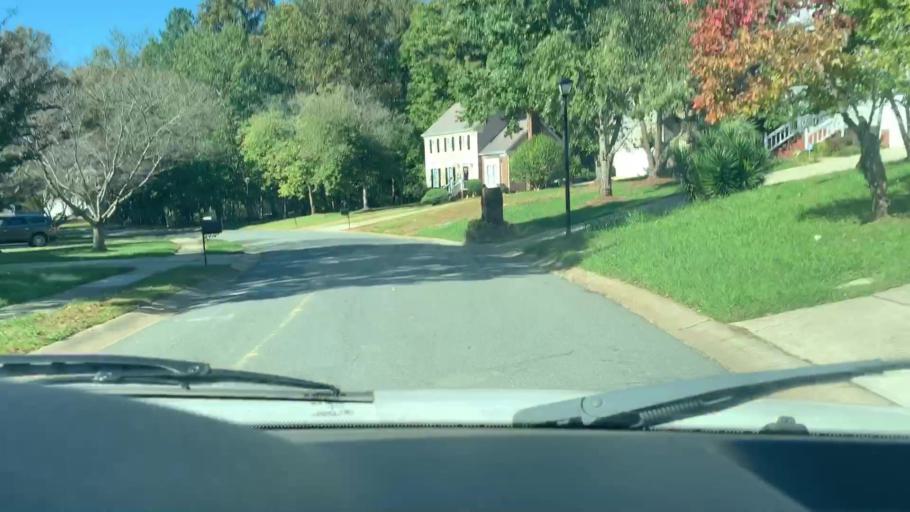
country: US
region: North Carolina
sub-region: Mecklenburg County
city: Charlotte
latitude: 35.2939
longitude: -80.7883
